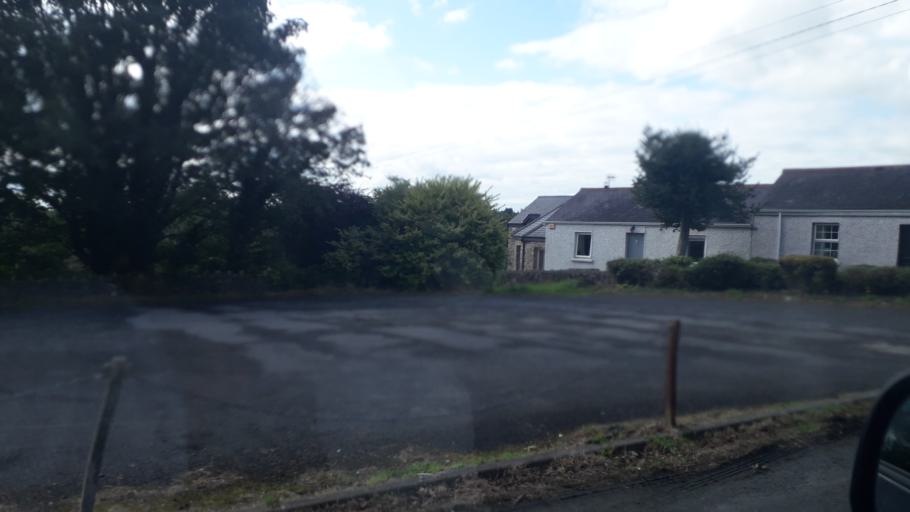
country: IE
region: Leinster
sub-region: Lu
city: Blackrock
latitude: 54.0436
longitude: -6.3320
